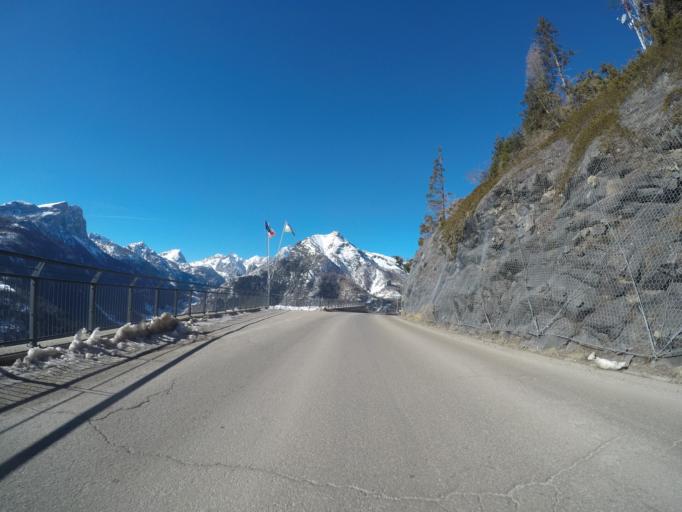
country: IT
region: Veneto
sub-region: Provincia di Belluno
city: Colle Santa Lucia
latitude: 46.4435
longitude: 12.0024
